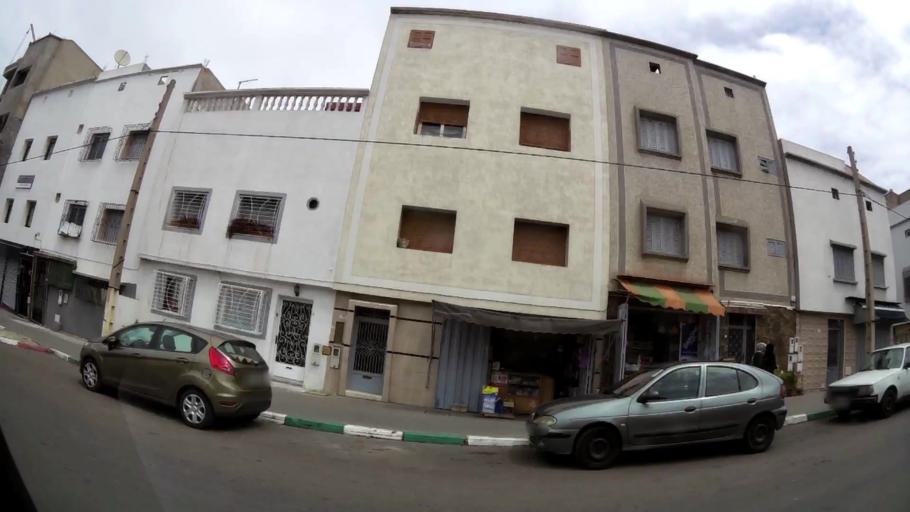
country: MA
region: Grand Casablanca
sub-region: Mediouna
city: Tit Mellil
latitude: 33.6116
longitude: -7.5016
